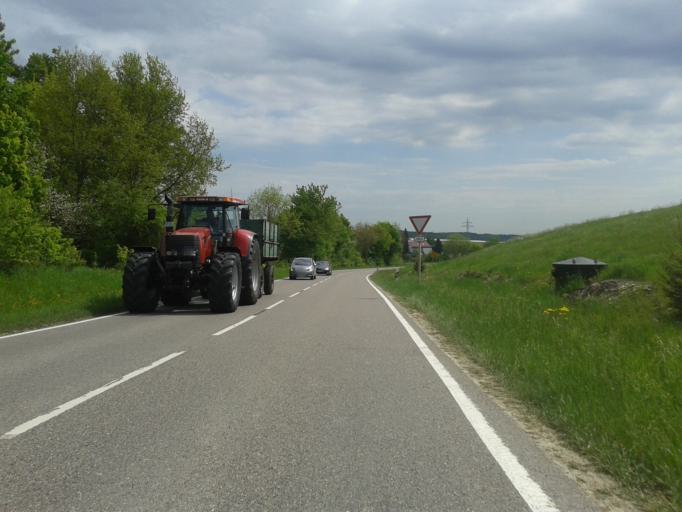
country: DE
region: Baden-Wuerttemberg
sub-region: Tuebingen Region
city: Erbach
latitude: 48.3572
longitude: 9.8762
